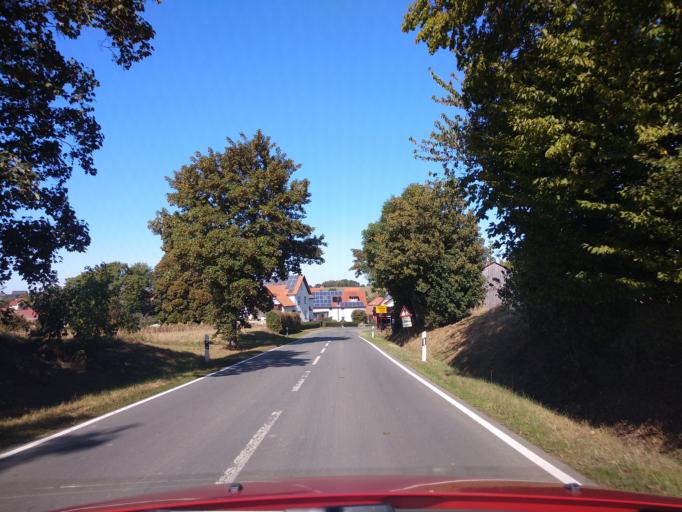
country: DE
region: Lower Saxony
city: Boffzen
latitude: 51.7470
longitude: 9.3069
